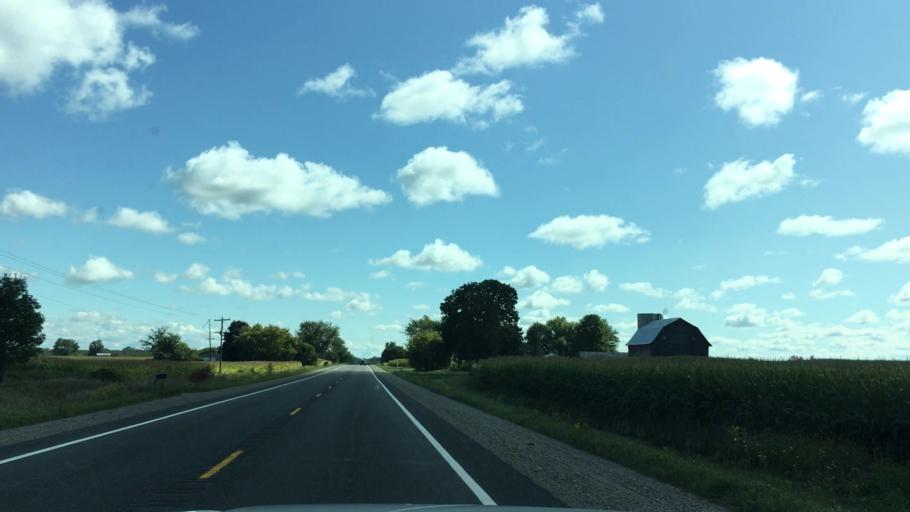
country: US
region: Michigan
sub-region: Montcalm County
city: Carson City
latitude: 43.1772
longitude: -84.8890
